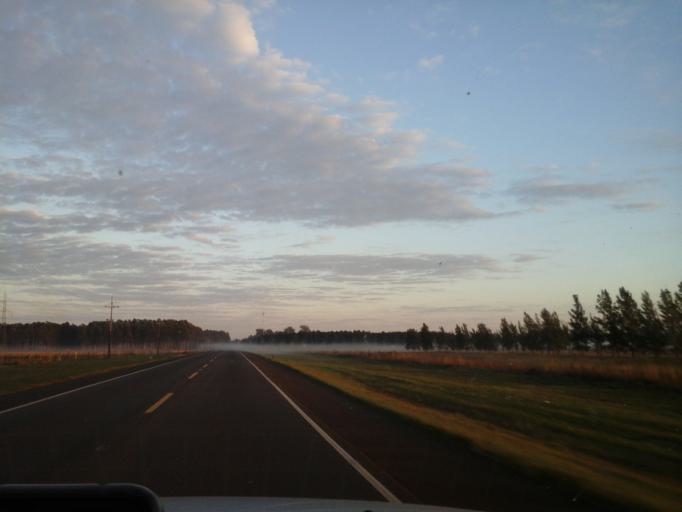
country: PY
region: Itapua
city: General Delgado
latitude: -27.0647
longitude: -56.6197
